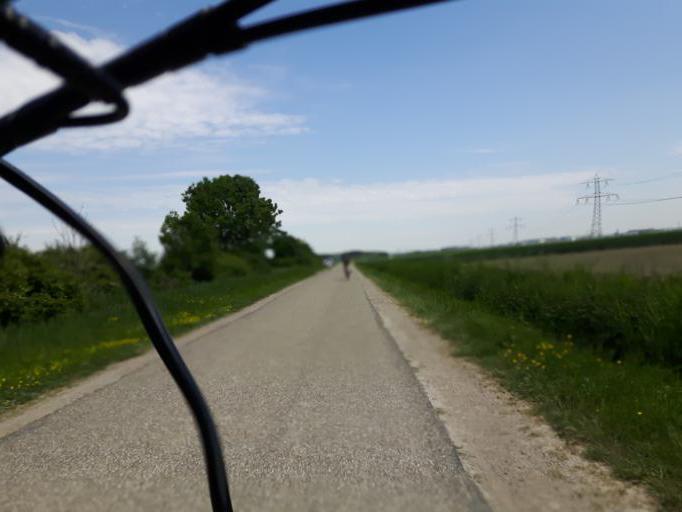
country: NL
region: Zeeland
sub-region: Gemeente Goes
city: Goes
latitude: 51.4787
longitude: 3.8452
